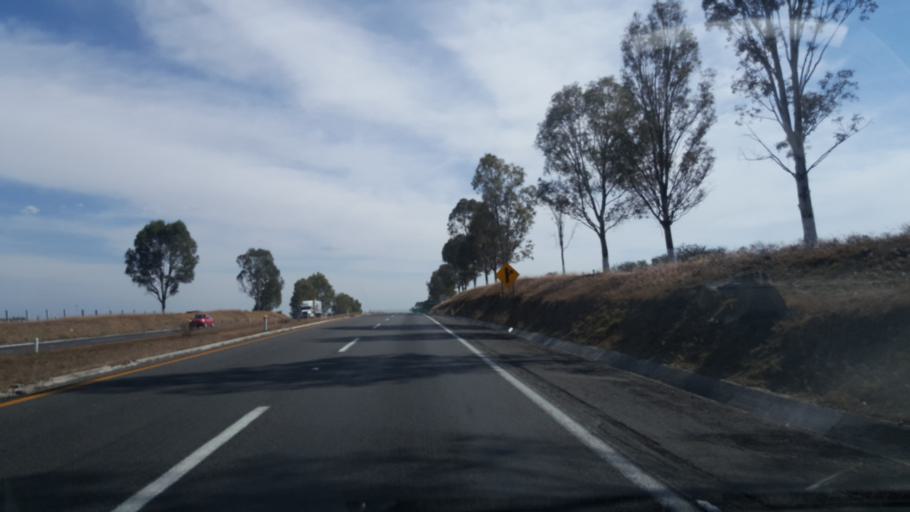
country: MX
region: Jalisco
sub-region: Lagos de Moreno
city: Cristeros [Fraccionamiento]
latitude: 21.2564
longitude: -101.9530
